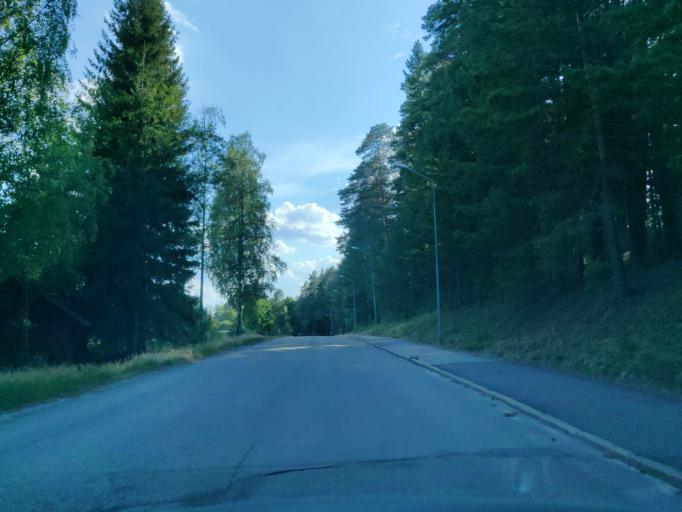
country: SE
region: Vaermland
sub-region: Hagfors Kommun
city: Hagfors
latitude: 60.0321
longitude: 13.7073
